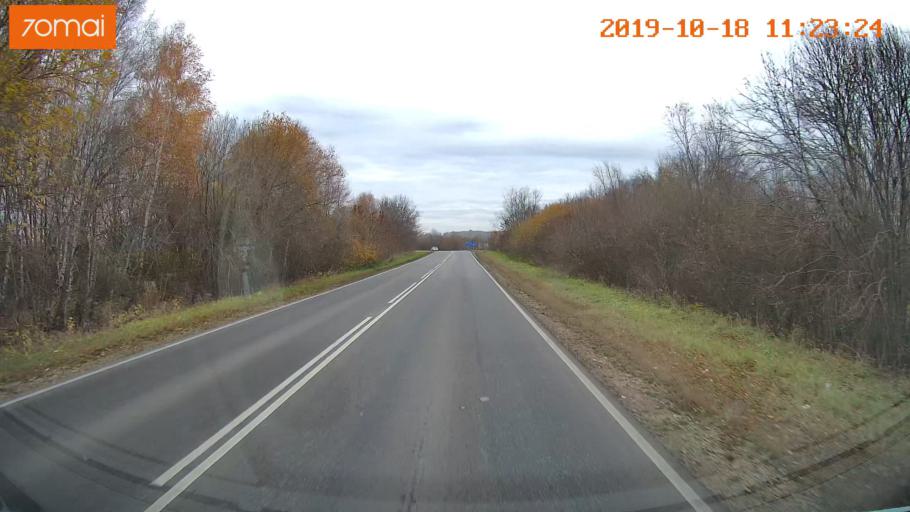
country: RU
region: Tula
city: Kimovsk
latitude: 54.1010
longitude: 38.5936
